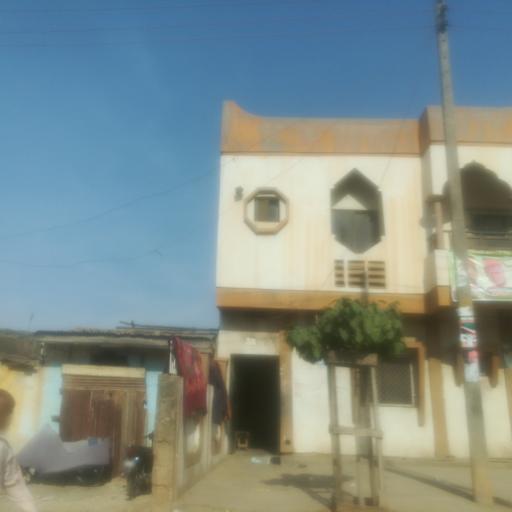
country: NG
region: Kano
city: Kano
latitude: 12.0101
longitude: 8.5286
